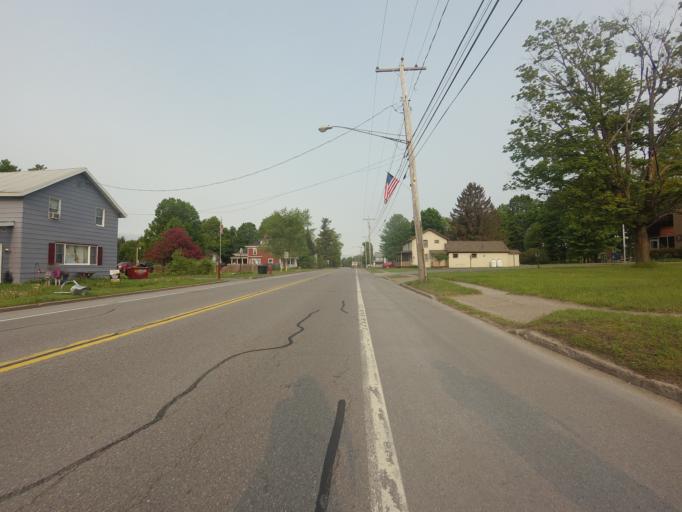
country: US
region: New York
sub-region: Jefferson County
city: Carthage
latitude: 44.0691
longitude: -75.4960
